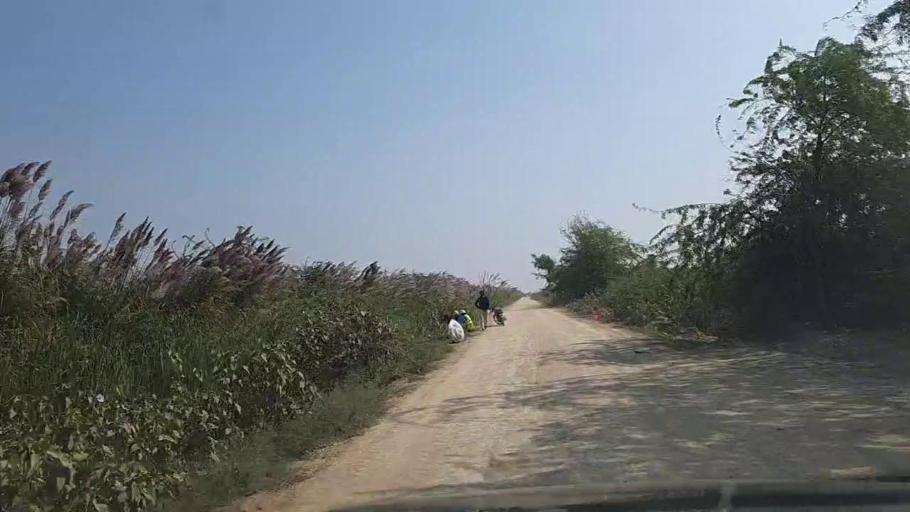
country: PK
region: Sindh
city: Gharo
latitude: 24.7202
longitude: 67.5586
